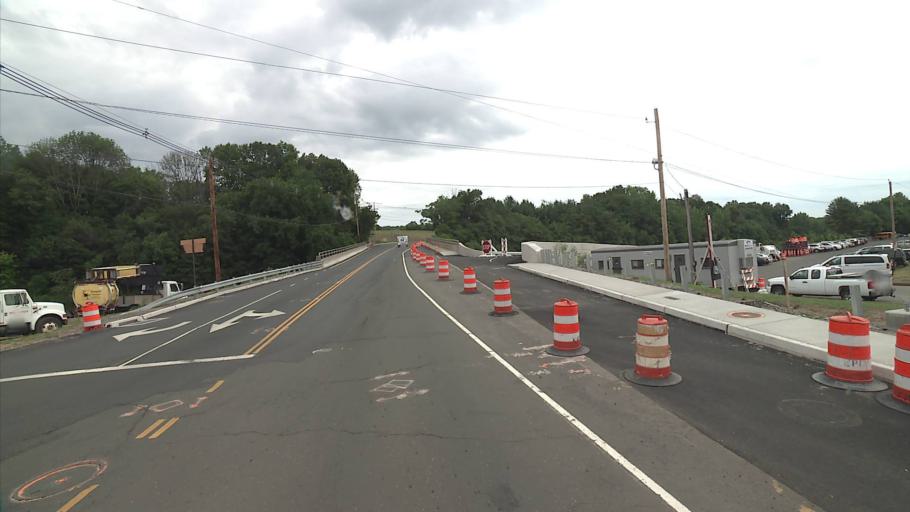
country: US
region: Connecticut
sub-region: New Haven County
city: Wallingford
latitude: 41.4615
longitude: -72.8333
